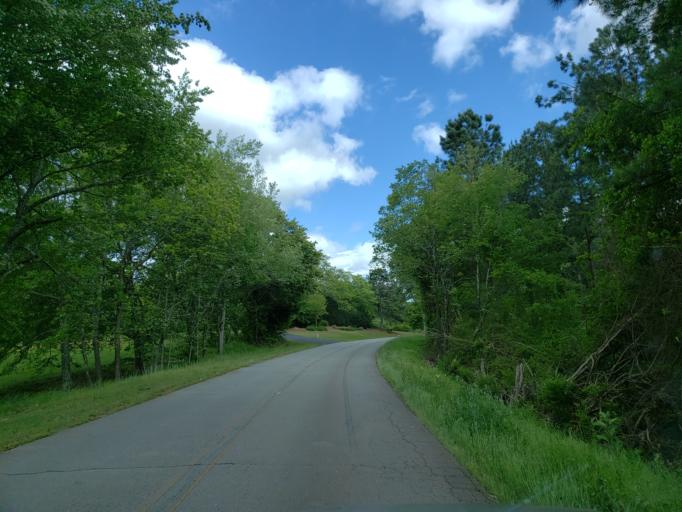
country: US
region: Georgia
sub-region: Carroll County
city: Mount Zion
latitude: 33.6473
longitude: -85.2808
